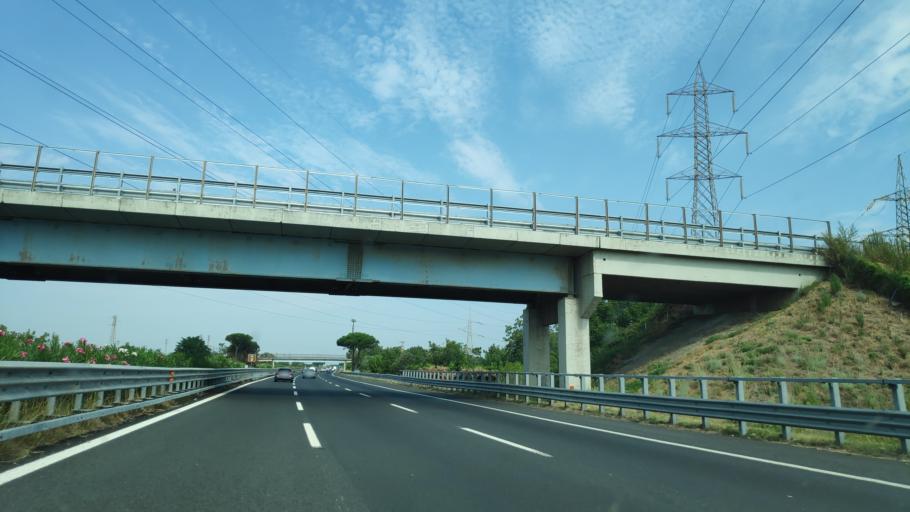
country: IT
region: Campania
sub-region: Provincia di Caserta
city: Maddaloni
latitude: 41.0159
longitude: 14.3724
